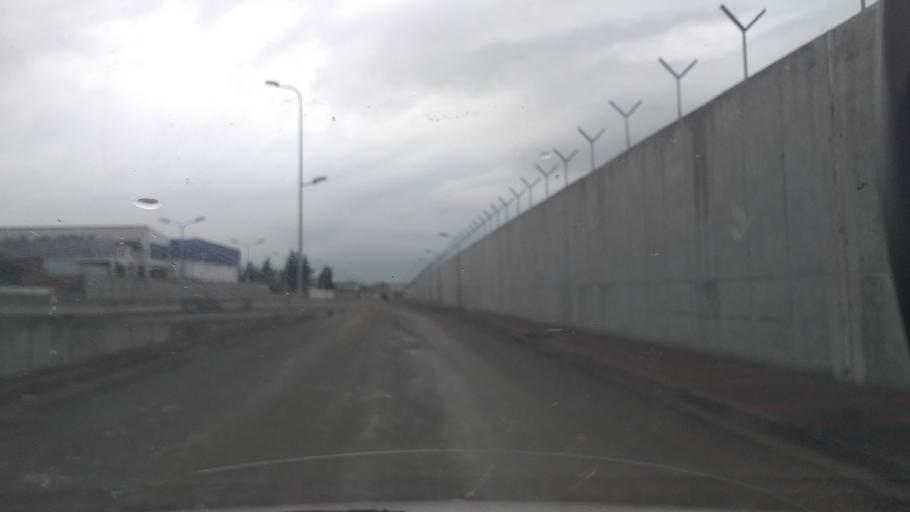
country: TN
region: Ariana
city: Ariana
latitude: 36.8530
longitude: 10.2124
